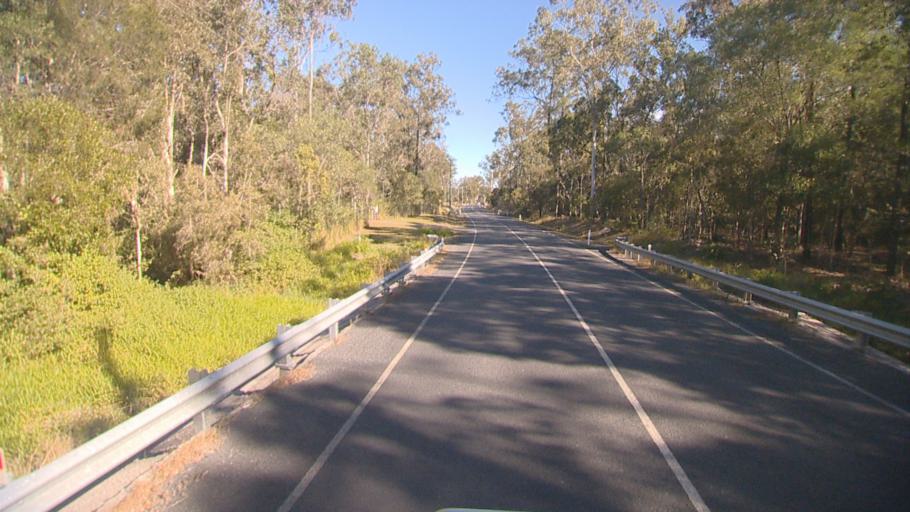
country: AU
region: Queensland
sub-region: Logan
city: North Maclean
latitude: -27.8090
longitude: 153.0586
